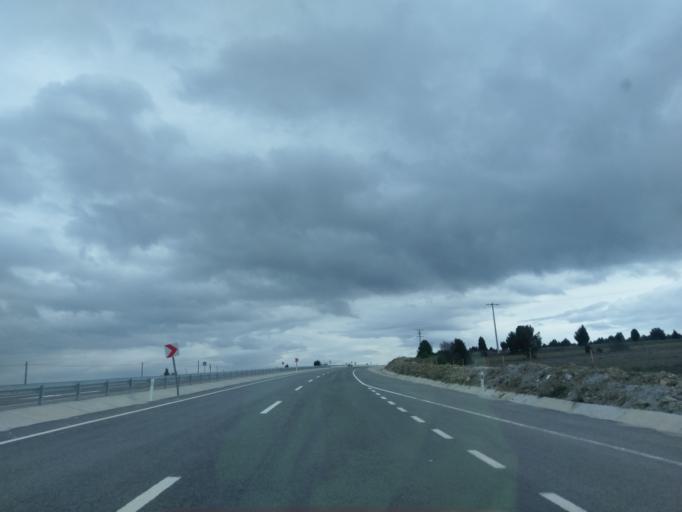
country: TR
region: Kuetahya
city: Cavdarhisar
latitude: 39.2264
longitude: 29.7140
